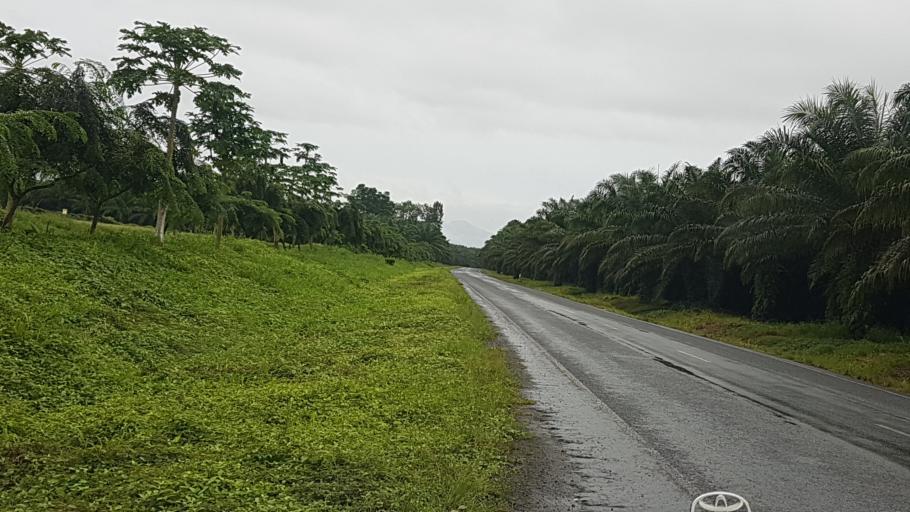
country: PG
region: Milne Bay
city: Alotau
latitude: -10.3225
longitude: 150.2811
